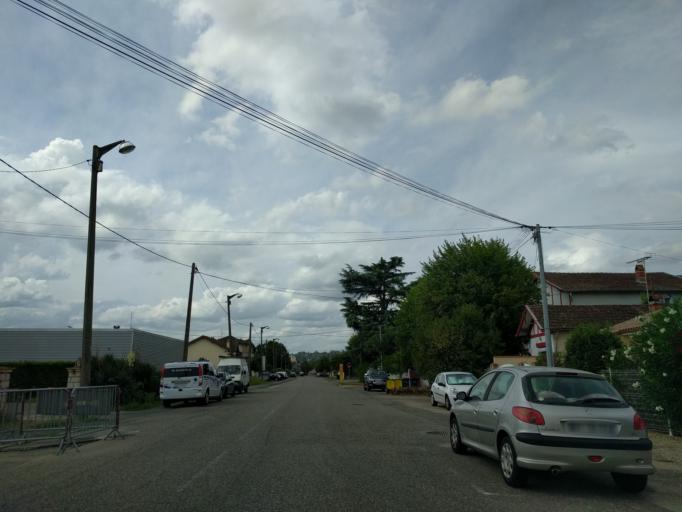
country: FR
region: Aquitaine
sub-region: Departement du Lot-et-Garonne
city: Agen
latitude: 44.1943
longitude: 0.6450
